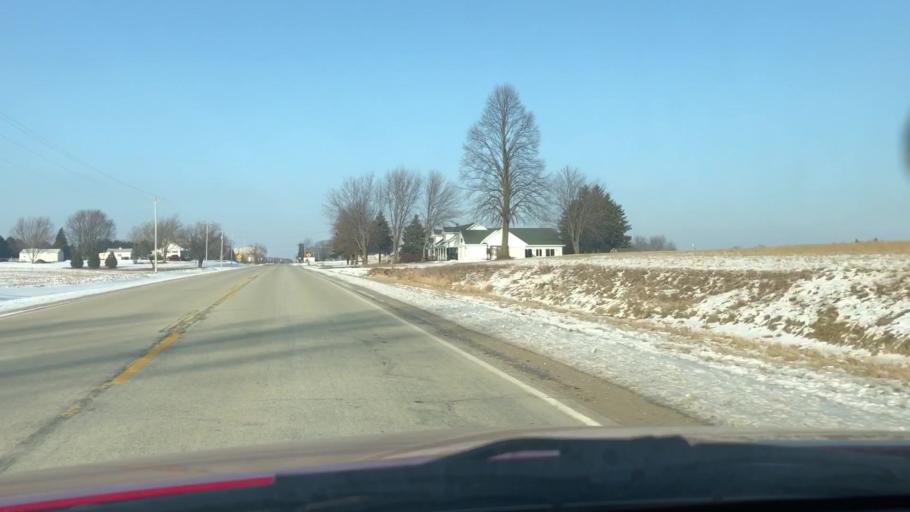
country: US
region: Wisconsin
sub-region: Outagamie County
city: Black Creek
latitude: 44.4105
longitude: -88.3742
